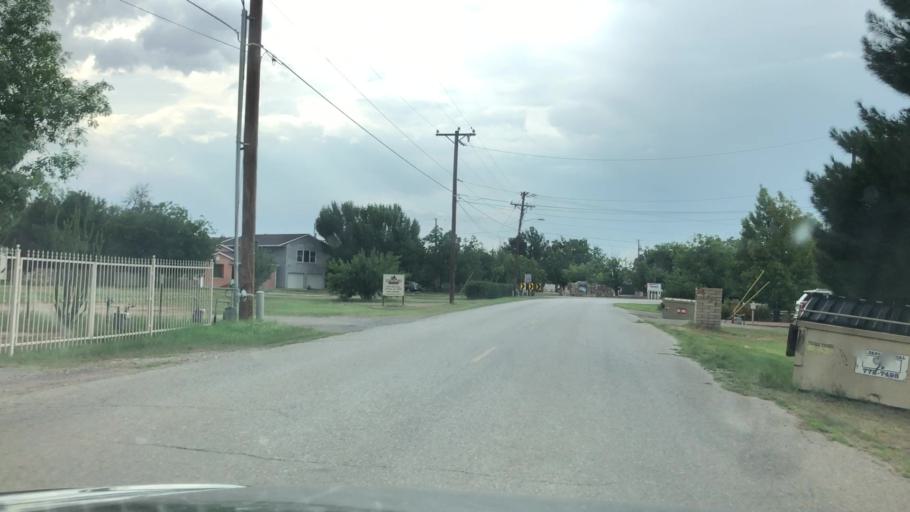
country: US
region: Texas
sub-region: El Paso County
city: Canutillo
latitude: 31.9039
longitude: -106.6396
